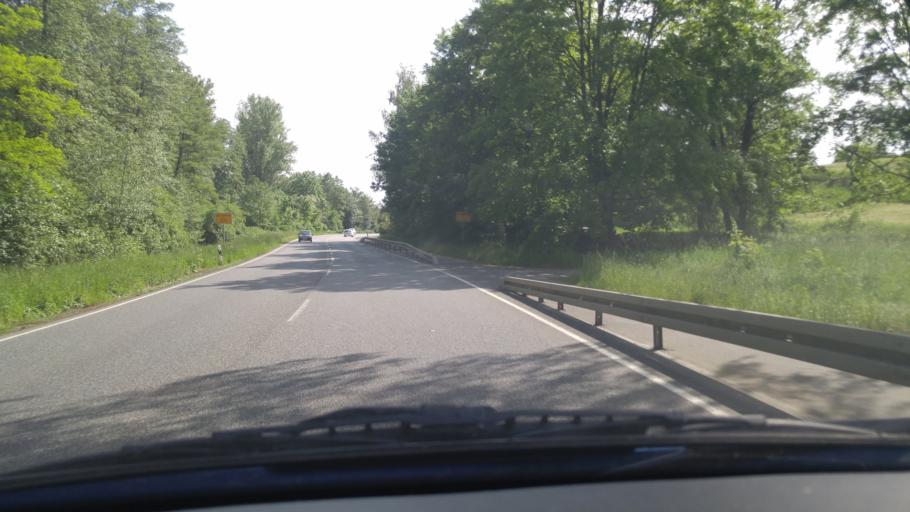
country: DE
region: Hesse
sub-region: Regierungsbezirk Darmstadt
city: Nidda
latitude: 50.4487
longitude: 9.0407
